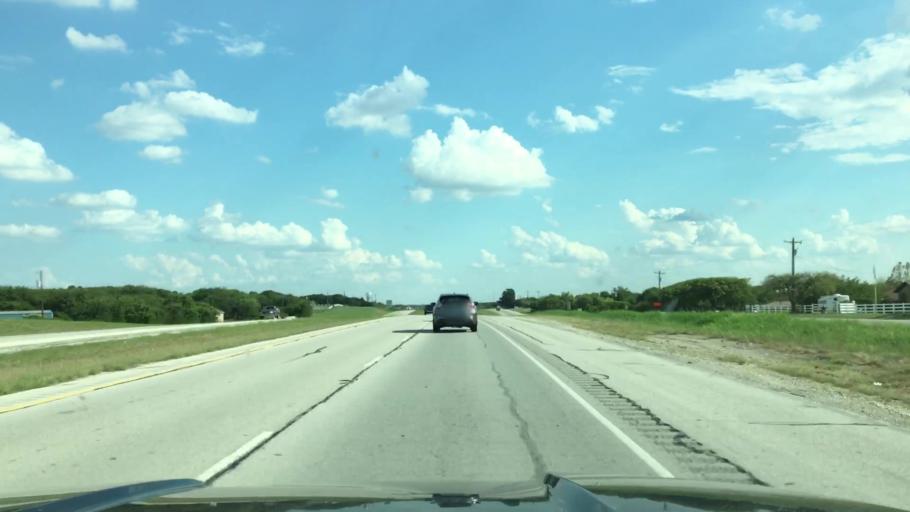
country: US
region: Texas
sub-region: Tarrant County
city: Pecan Acres
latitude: 32.9912
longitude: -97.4307
